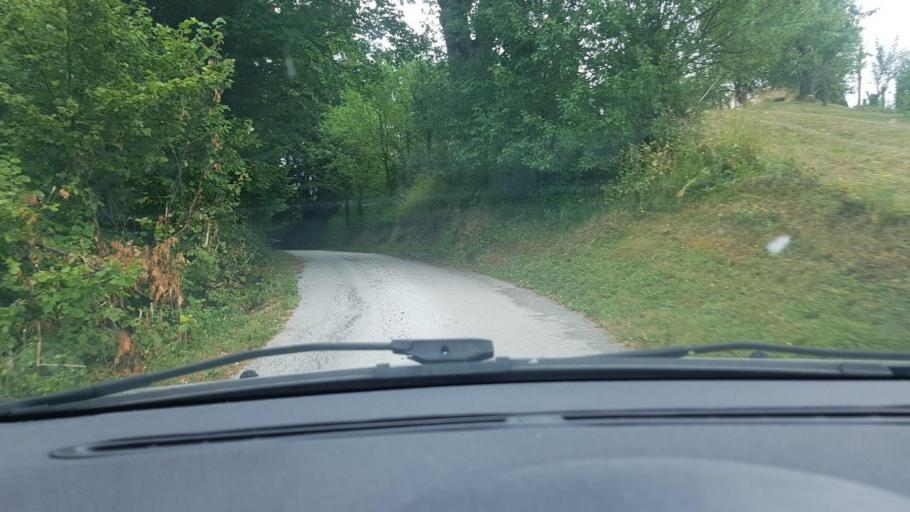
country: SI
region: Videm
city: Videm pri Ptuju
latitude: 46.3367
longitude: 15.9141
